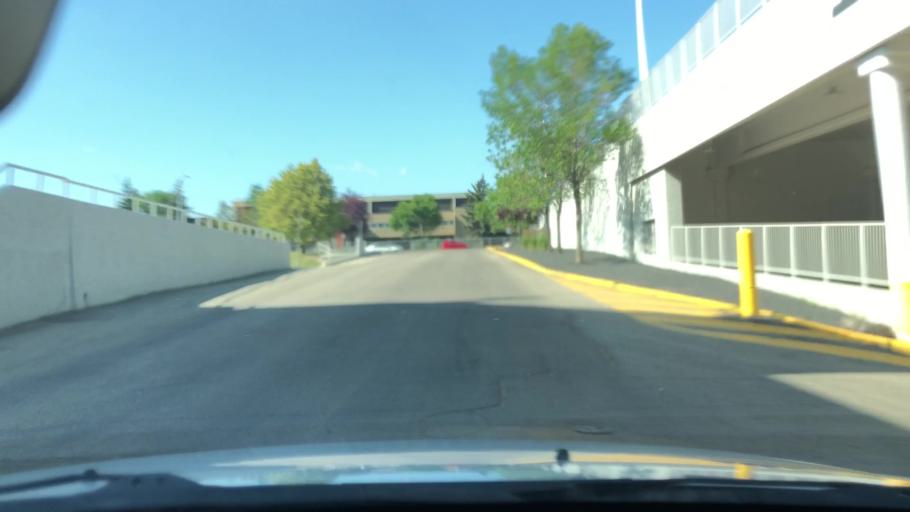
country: CA
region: Alberta
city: Edmonton
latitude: 53.6039
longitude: -113.4443
